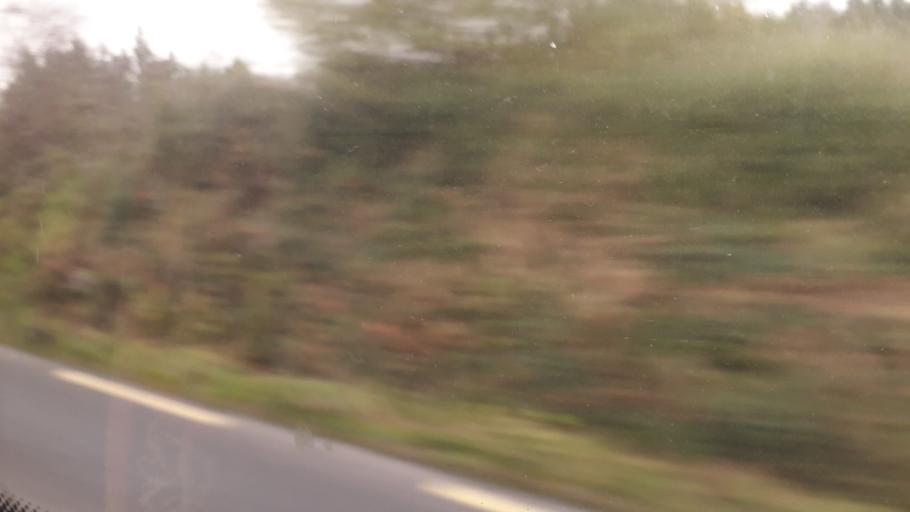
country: IE
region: Munster
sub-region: An Clar
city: Ennis
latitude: 52.8721
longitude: -9.1690
